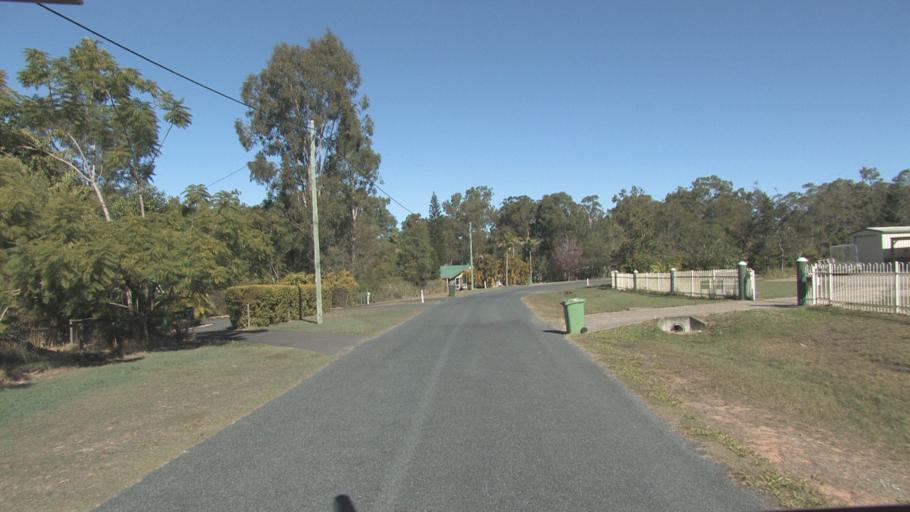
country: AU
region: Queensland
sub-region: Logan
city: Park Ridge South
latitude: -27.7285
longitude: 153.0474
